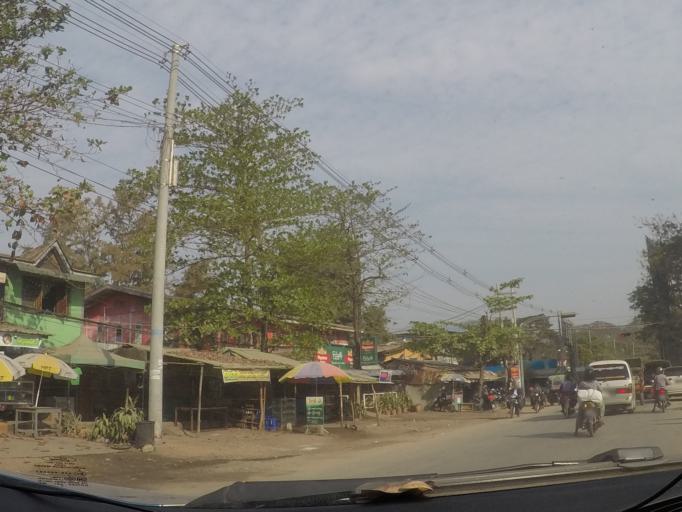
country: MM
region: Bago
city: Pyay
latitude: 18.8192
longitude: 95.2503
